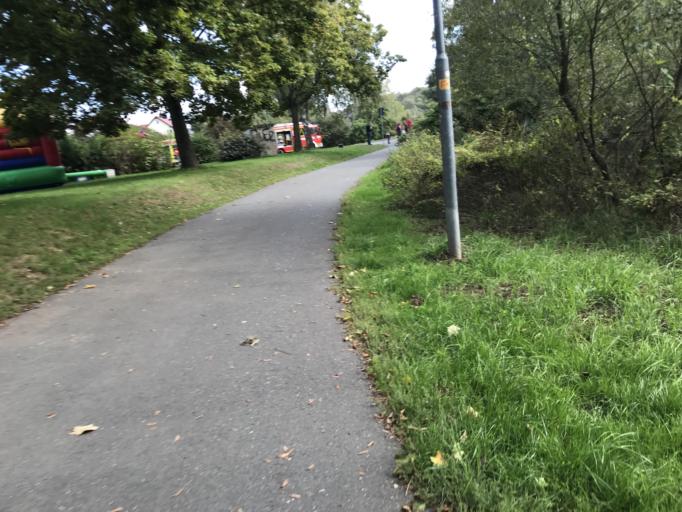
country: DE
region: Hesse
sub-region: Regierungsbezirk Giessen
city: Ehringshausen
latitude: 50.5952
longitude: 8.4161
